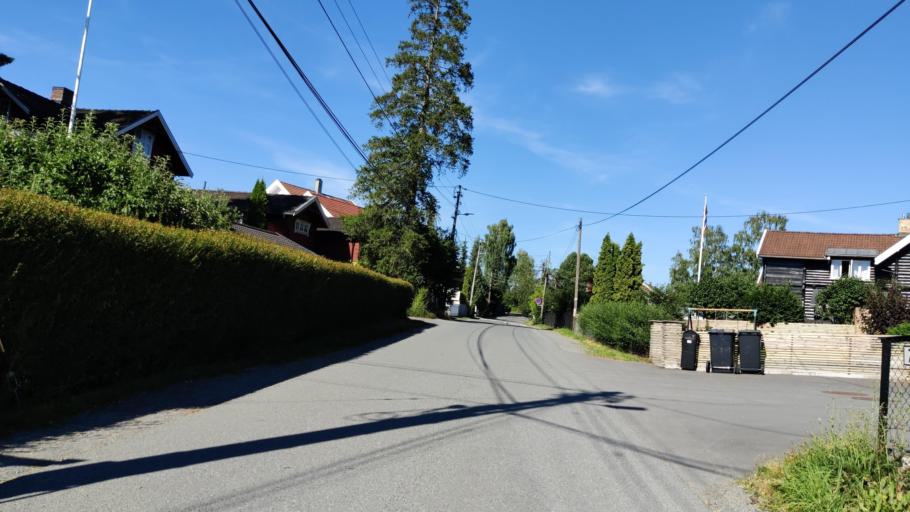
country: NO
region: Akershus
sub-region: Baerum
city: Lysaker
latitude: 59.9202
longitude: 10.5916
